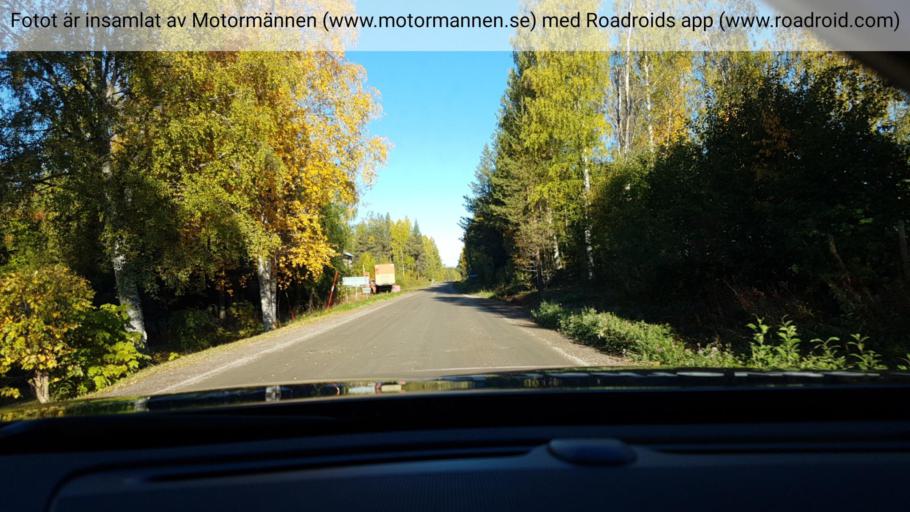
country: SE
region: Norrbotten
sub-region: Alvsbyns Kommun
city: AElvsbyn
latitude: 66.1956
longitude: 21.1874
